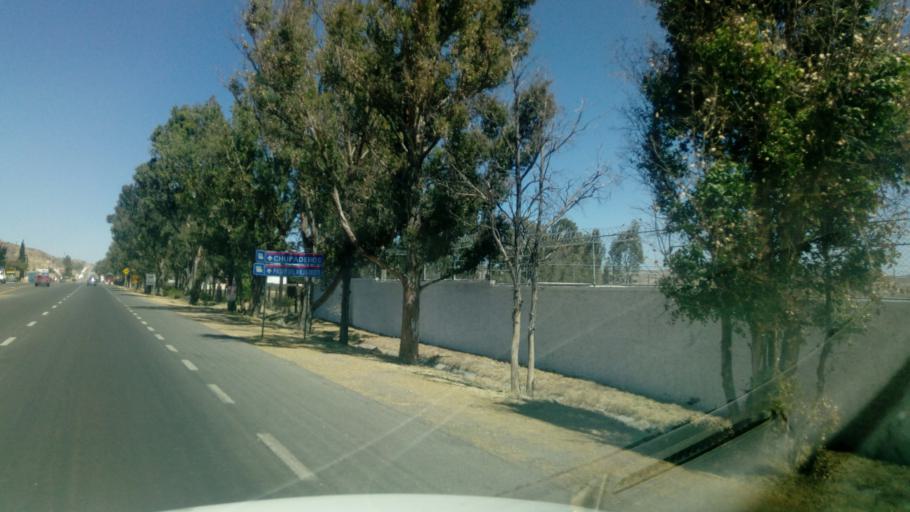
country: MX
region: Durango
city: Victoria de Durango
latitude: 24.0758
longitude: -104.6630
